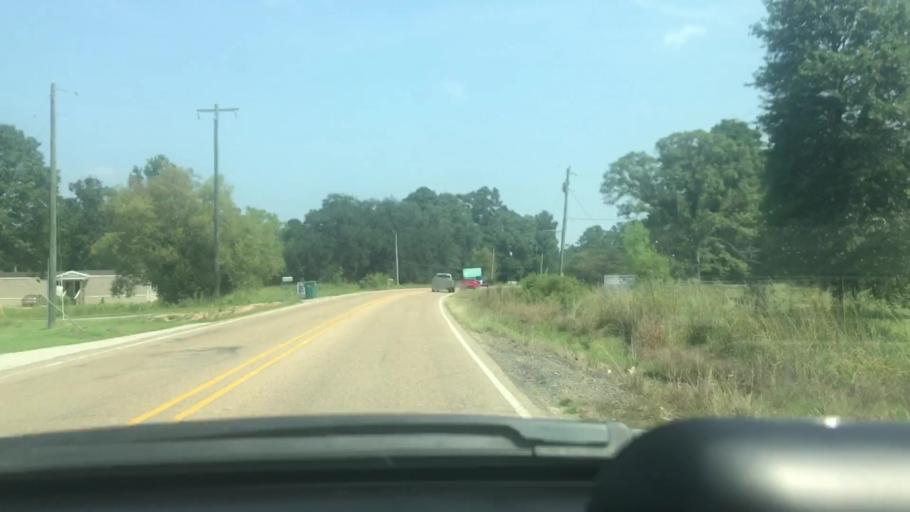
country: US
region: Louisiana
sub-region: Livingston Parish
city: Denham Springs
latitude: 30.4740
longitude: -90.9190
